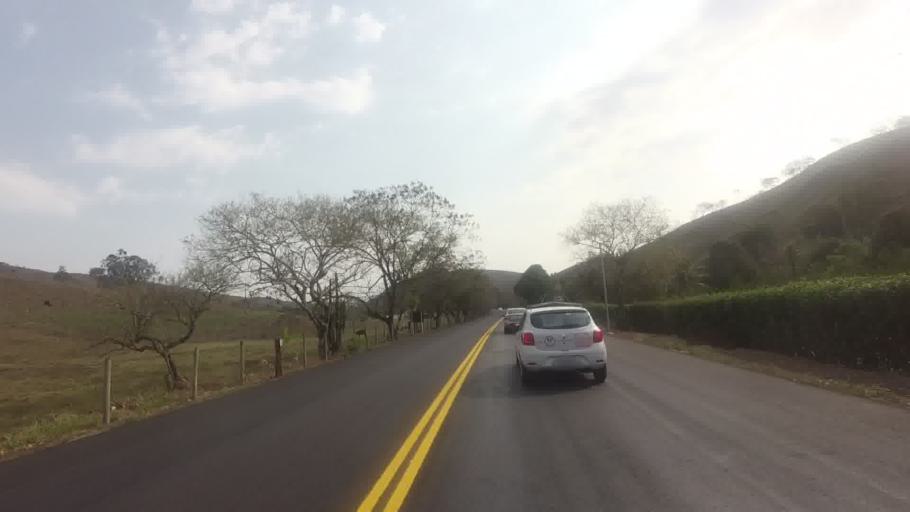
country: BR
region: Rio de Janeiro
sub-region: Bom Jesus Do Itabapoana
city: Bom Jesus do Itabapoana
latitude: -21.2221
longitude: -41.7401
